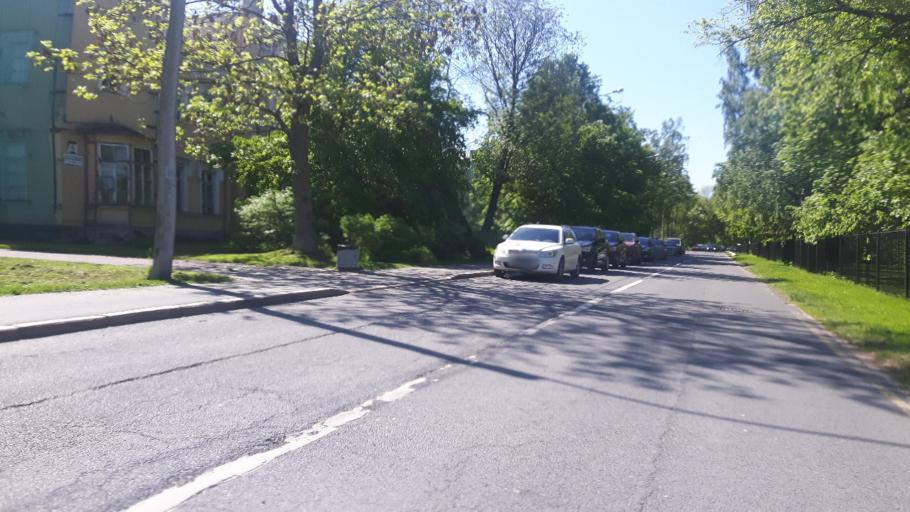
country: RU
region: St.-Petersburg
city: Peterhof
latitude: 59.8809
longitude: 29.9240
